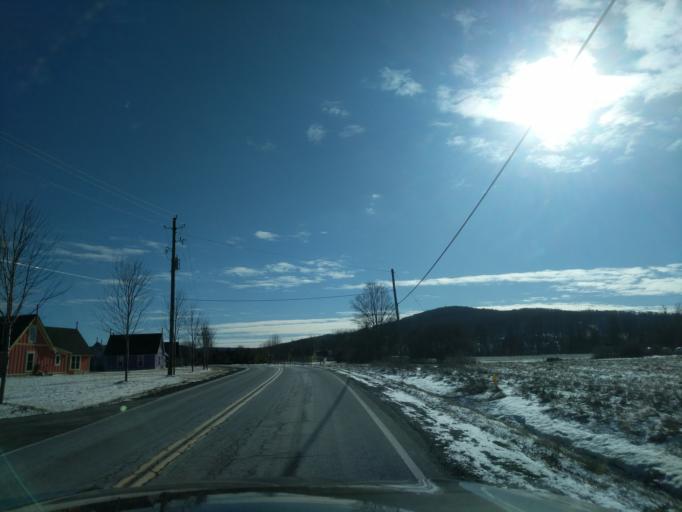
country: US
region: New York
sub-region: Tompkins County
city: Dryden
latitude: 42.3902
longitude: -76.3625
